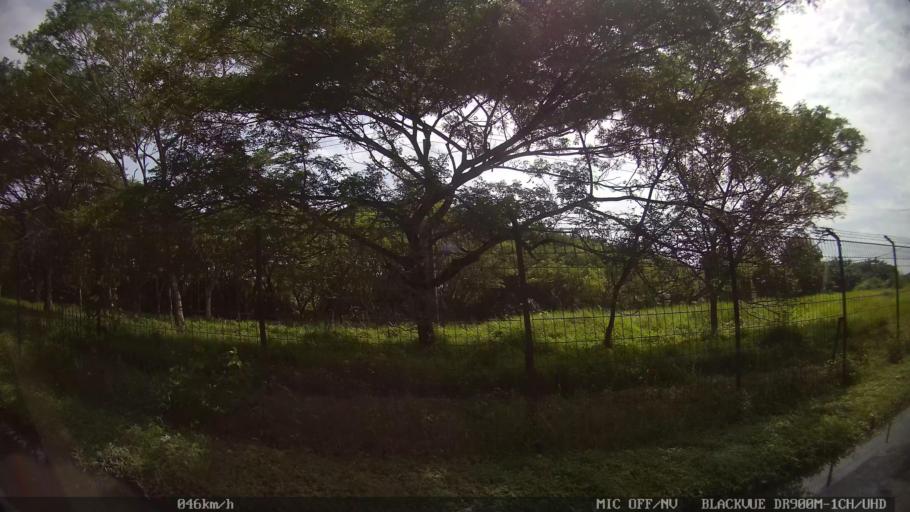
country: ID
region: North Sumatra
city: Percut
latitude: 3.6052
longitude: 98.8597
